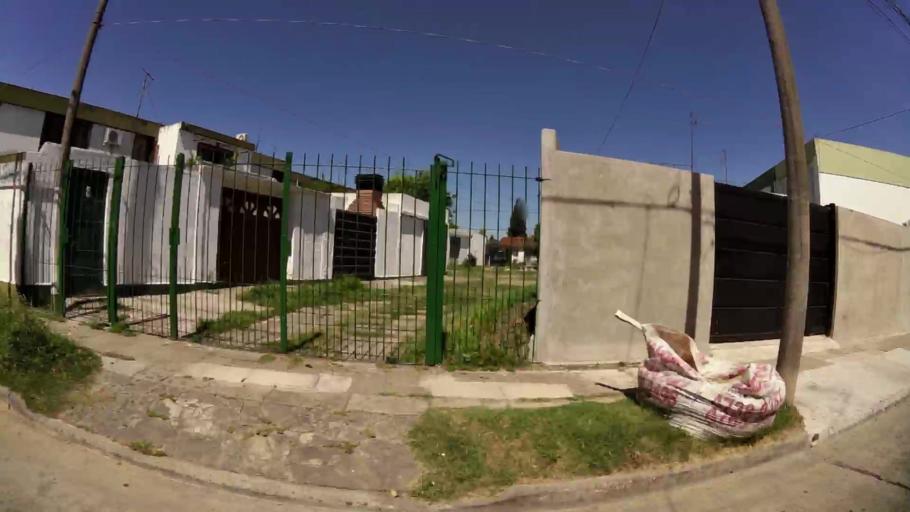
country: AR
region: Buenos Aires
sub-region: Partido de General San Martin
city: General San Martin
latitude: -34.5609
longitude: -58.5526
